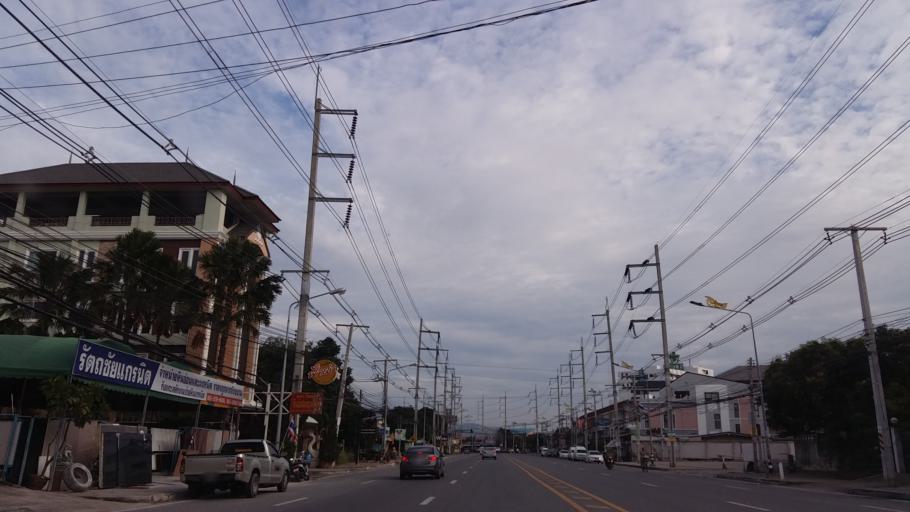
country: TH
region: Chon Buri
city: Chon Buri
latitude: 13.3207
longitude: 100.9467
